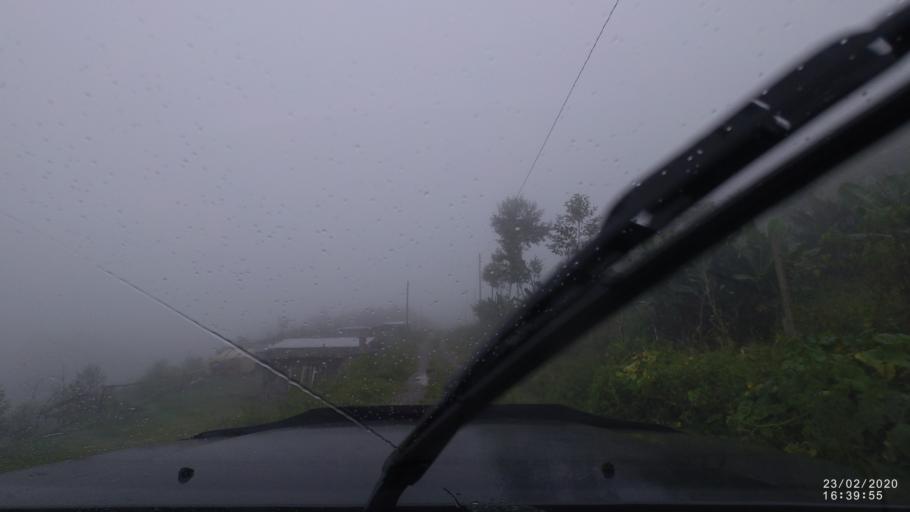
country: BO
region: Cochabamba
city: Colomi
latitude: -17.0855
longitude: -66.0009
